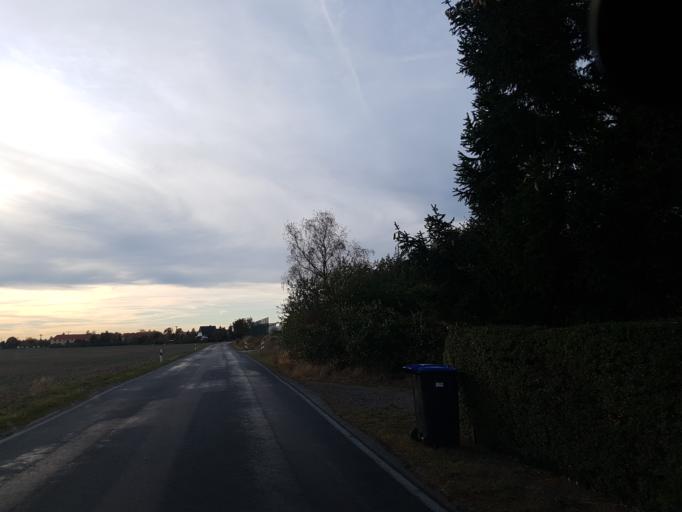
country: DE
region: Saxony
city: Wulknitz
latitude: 51.3668
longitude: 13.3992
